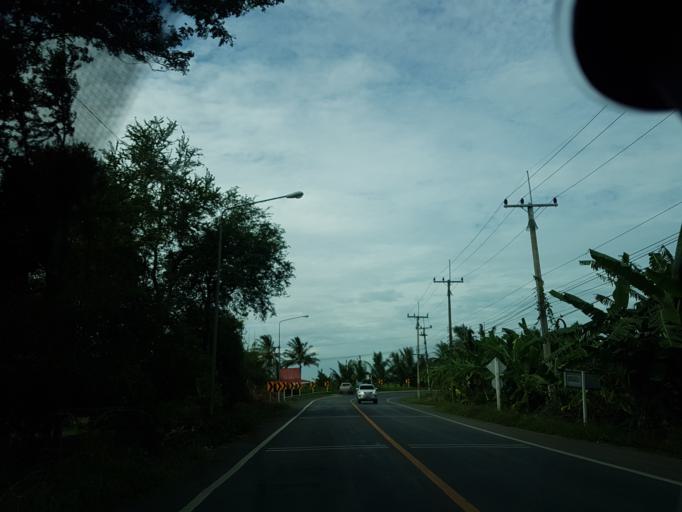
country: TH
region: Lop Buri
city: Tha Wung
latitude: 14.7432
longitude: 100.5428
